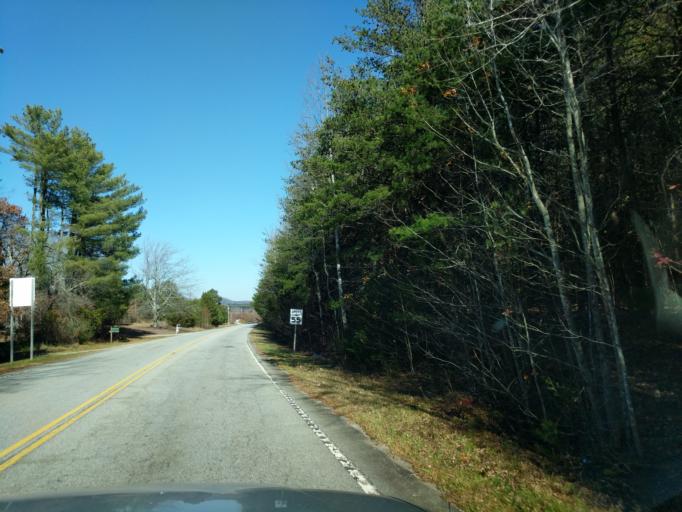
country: US
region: South Carolina
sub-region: Spartanburg County
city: Landrum
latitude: 35.1196
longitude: -82.2252
